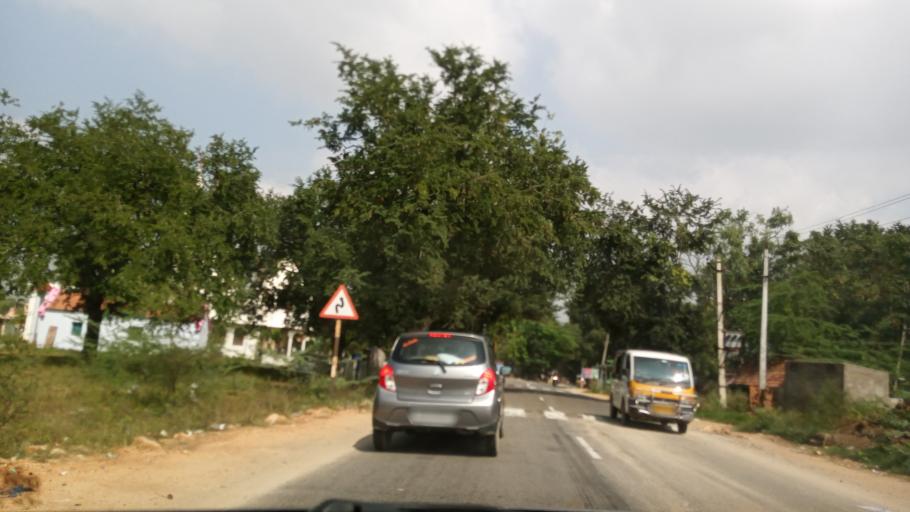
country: IN
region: Andhra Pradesh
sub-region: Chittoor
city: Madanapalle
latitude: 13.6297
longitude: 78.5520
